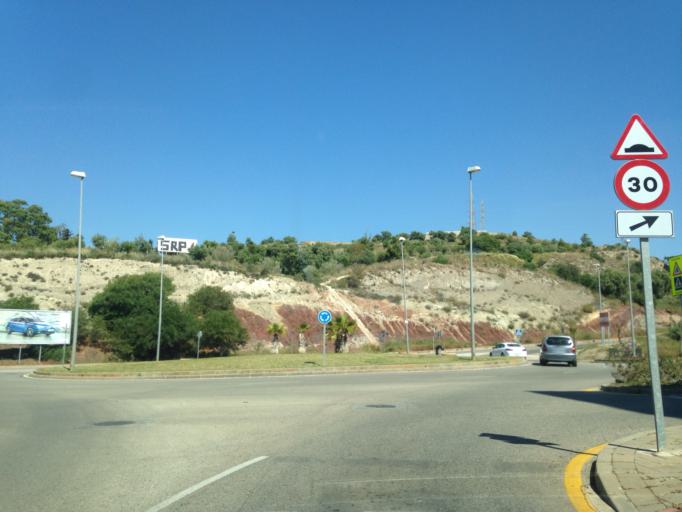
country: ES
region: Andalusia
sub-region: Provincia de Malaga
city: Malaga
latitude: 36.7253
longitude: -4.4847
